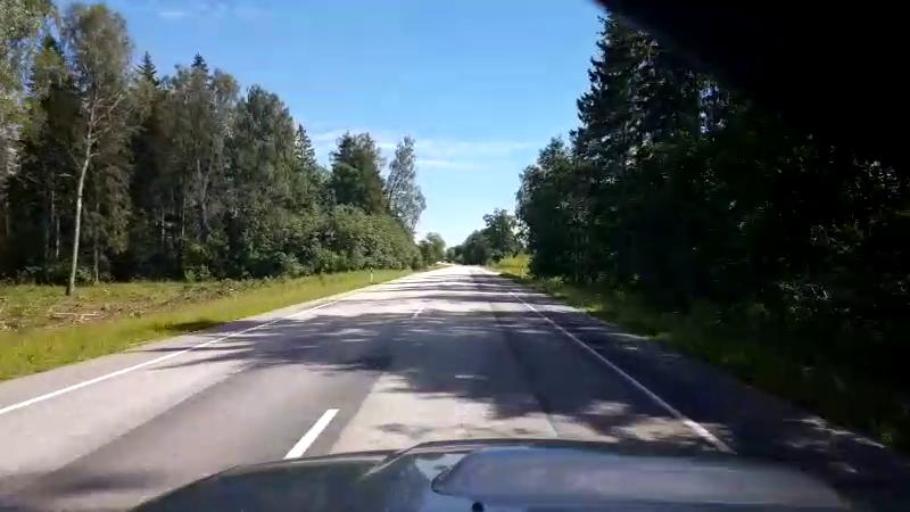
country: EE
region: Jaervamaa
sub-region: Koeru vald
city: Koeru
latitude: 58.9930
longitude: 25.9596
